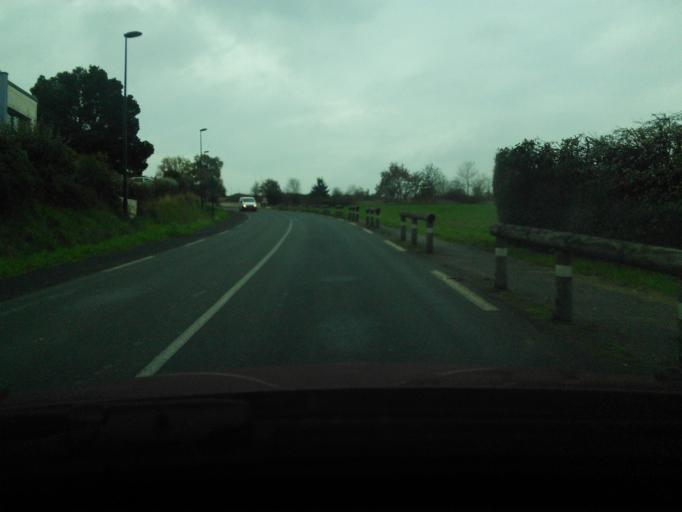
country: FR
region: Brittany
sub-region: Departement des Cotes-d'Armor
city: Yffiniac
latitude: 48.4825
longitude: -2.6820
